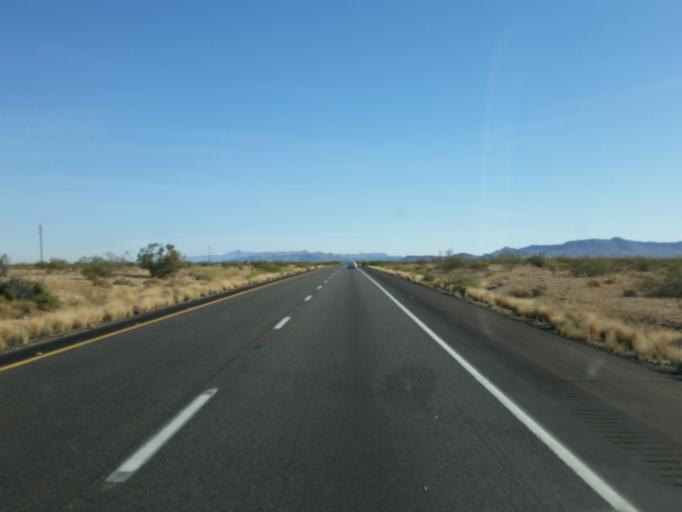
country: US
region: Arizona
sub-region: Mohave County
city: Kingman
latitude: 34.9859
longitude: -114.1390
